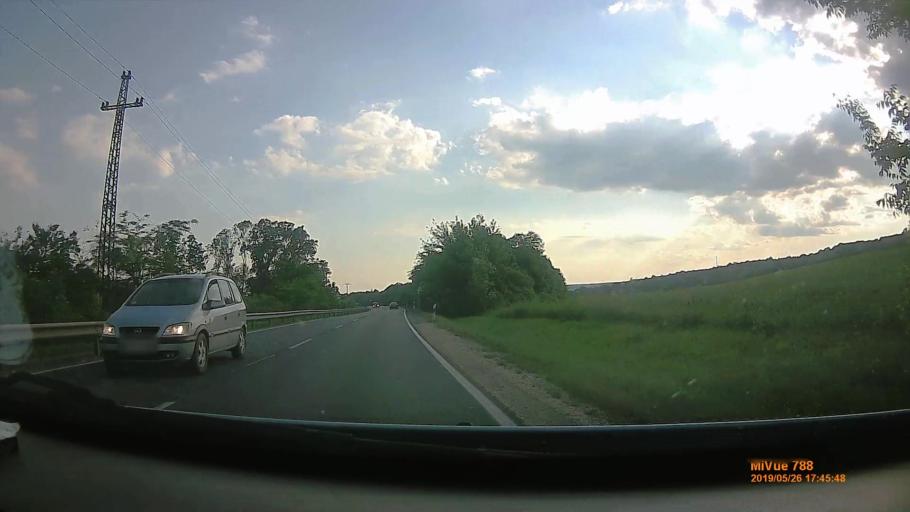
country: HU
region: Borsod-Abauj-Zemplen
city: Szikszo
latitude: 48.2142
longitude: 20.9451
